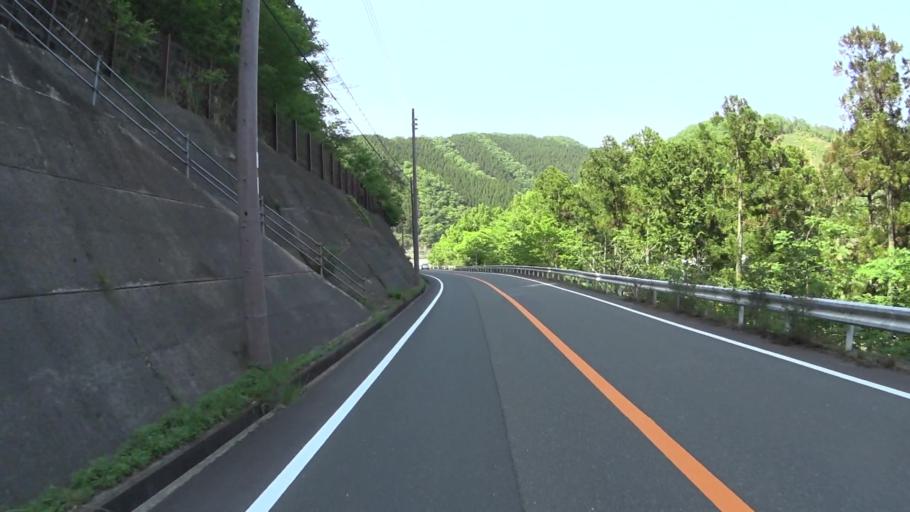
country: JP
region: Kyoto
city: Kameoka
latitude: 35.1484
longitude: 135.5125
